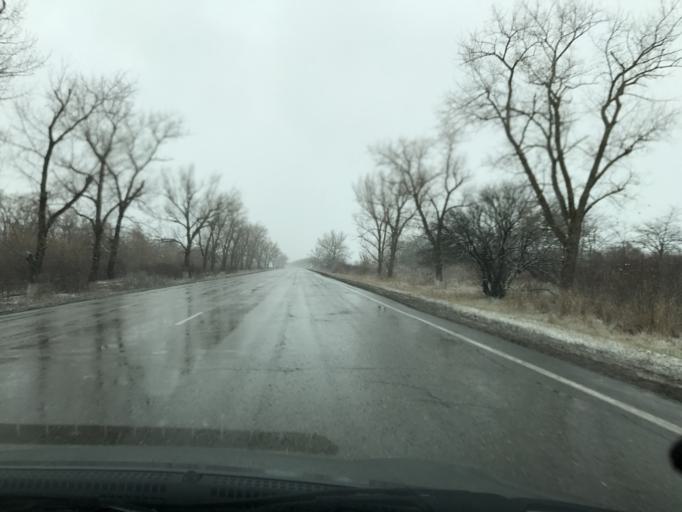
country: RU
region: Rostov
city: Kirovskaya
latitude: 47.0083
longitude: 39.9478
